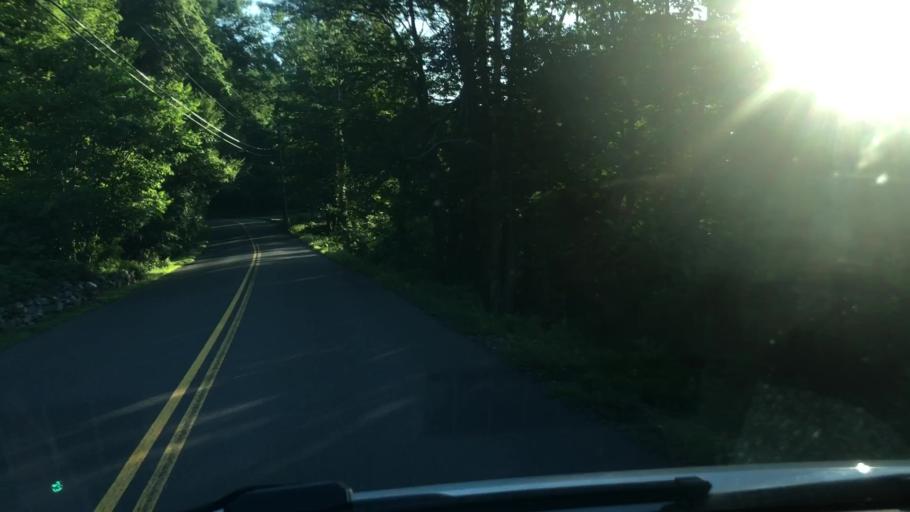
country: US
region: Massachusetts
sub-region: Hampshire County
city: Williamsburg
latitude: 42.3427
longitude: -72.7230
